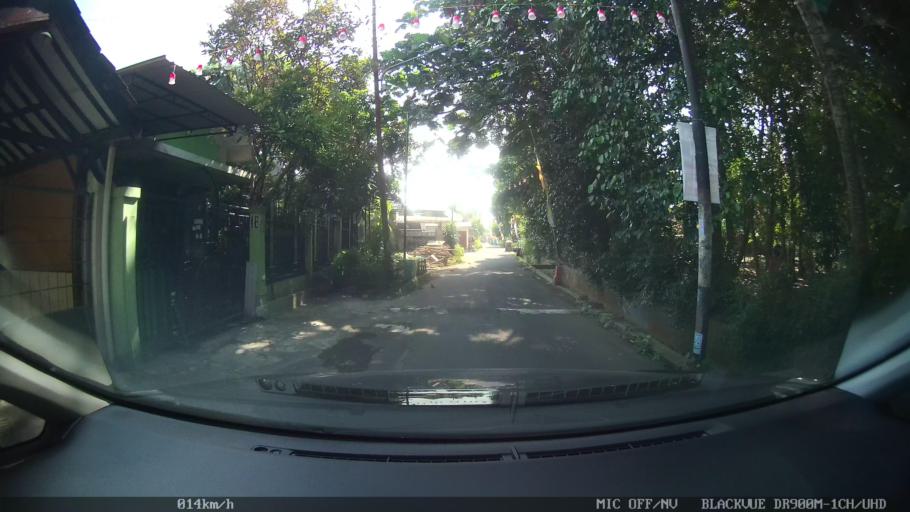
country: ID
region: Daerah Istimewa Yogyakarta
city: Sewon
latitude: -7.8312
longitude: 110.3924
